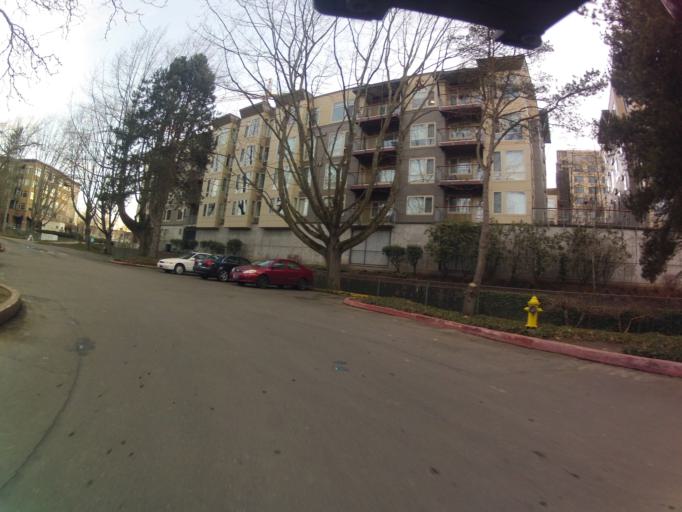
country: US
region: Washington
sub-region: King County
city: Renton
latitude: 47.5034
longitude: -122.2028
